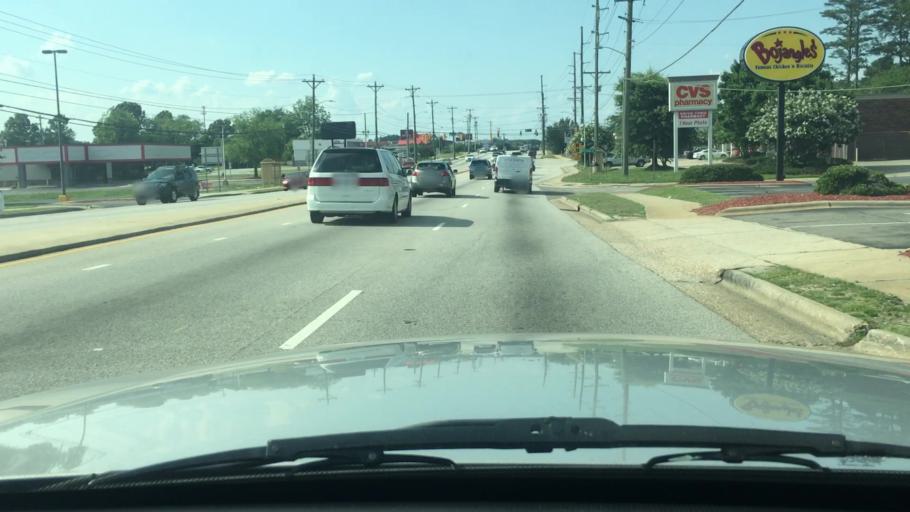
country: US
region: North Carolina
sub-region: Cumberland County
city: Fayetteville
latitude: 35.1063
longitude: -78.8785
